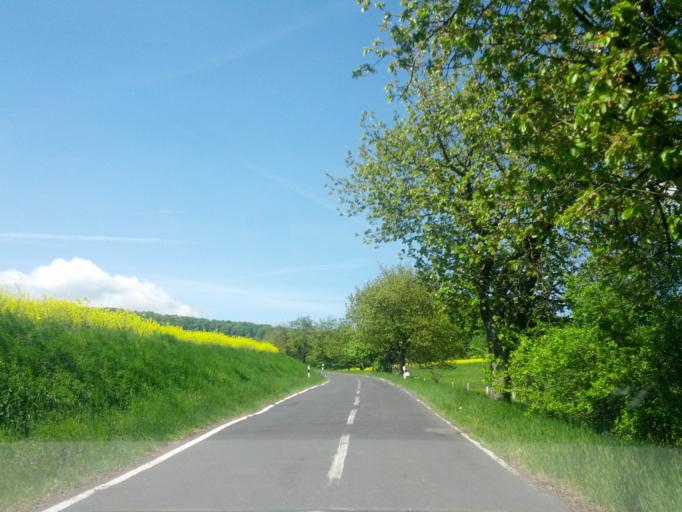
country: DE
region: Thuringia
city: Treffurt
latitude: 51.1070
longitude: 10.2154
